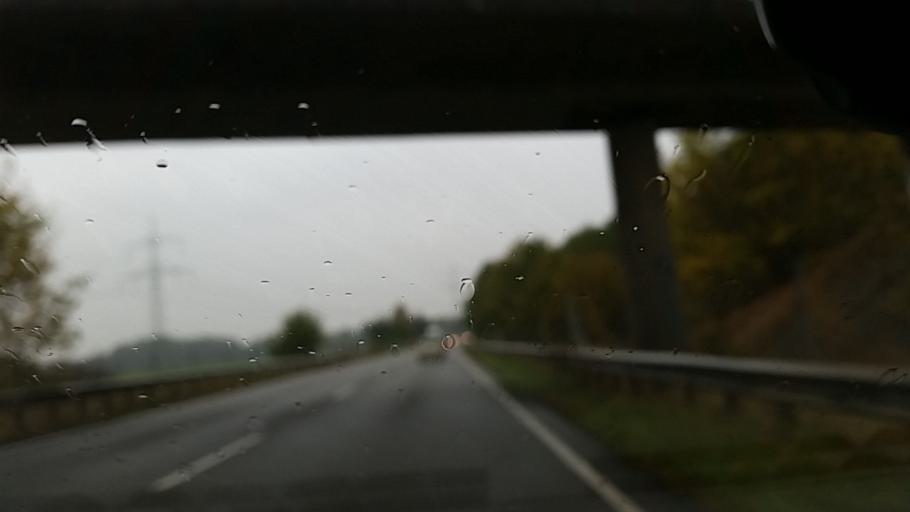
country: DE
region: Lower Saxony
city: Handorf
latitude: 53.3444
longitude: 10.3359
